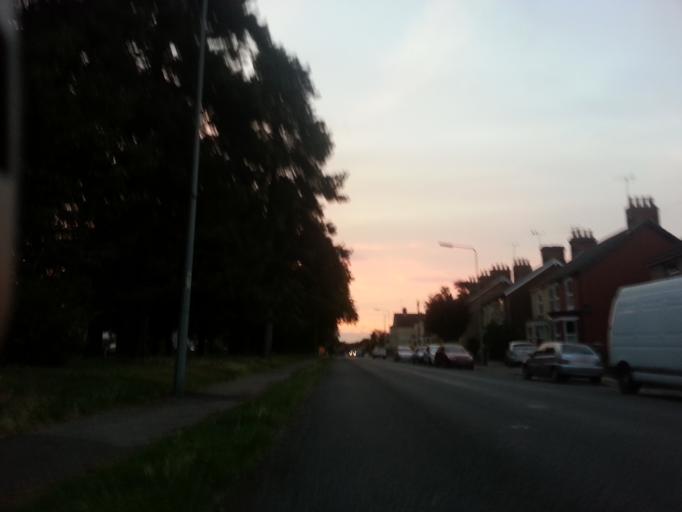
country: GB
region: England
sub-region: Suffolk
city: Ipswich
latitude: 52.0457
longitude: 1.1790
